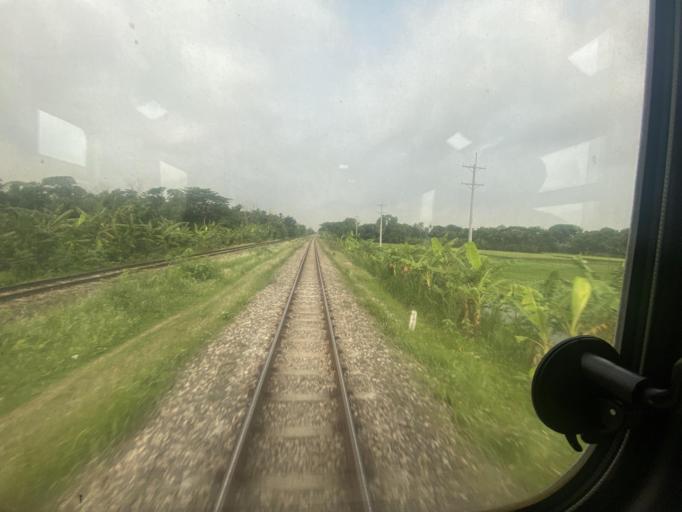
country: BD
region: Dhaka
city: Tungi
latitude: 23.9298
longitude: 90.5405
